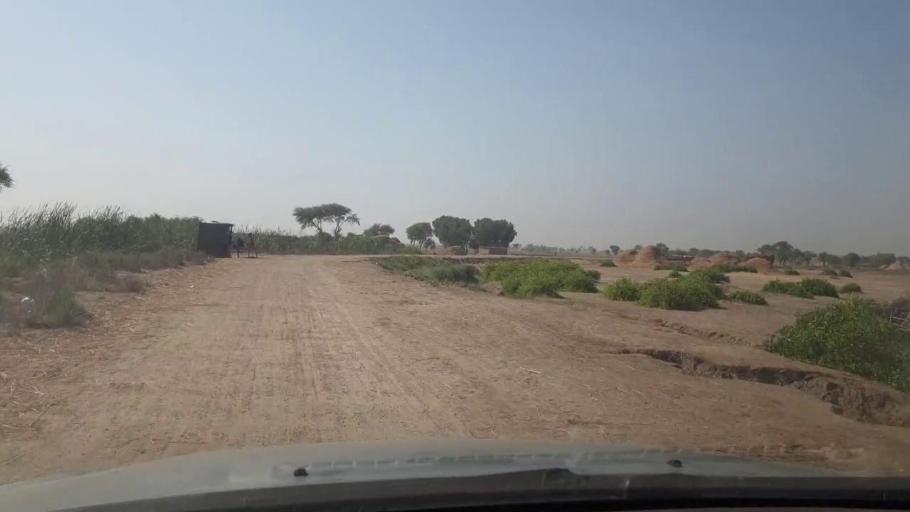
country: PK
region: Sindh
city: Bulri
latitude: 24.9064
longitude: 68.4344
